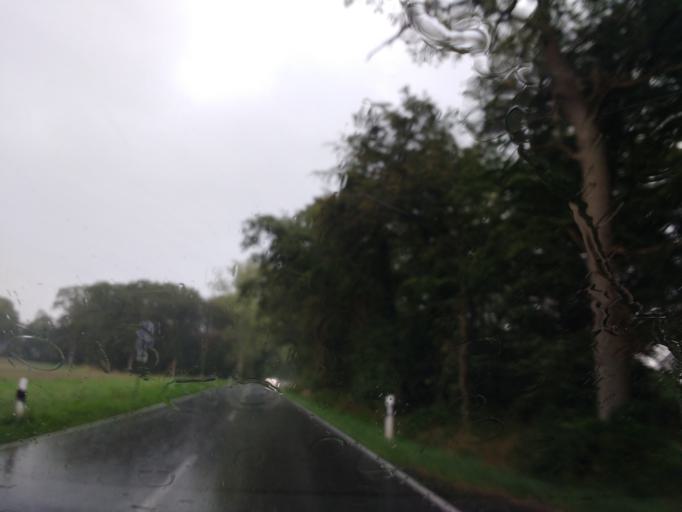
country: DE
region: North Rhine-Westphalia
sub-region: Regierungsbezirk Munster
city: Lienen
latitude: 52.1099
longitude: 7.9424
